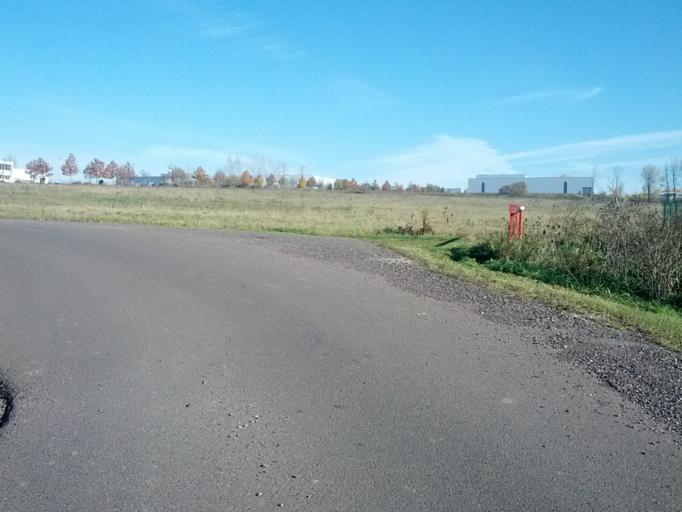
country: DE
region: Thuringia
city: Haina
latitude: 50.9995
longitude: 10.4380
